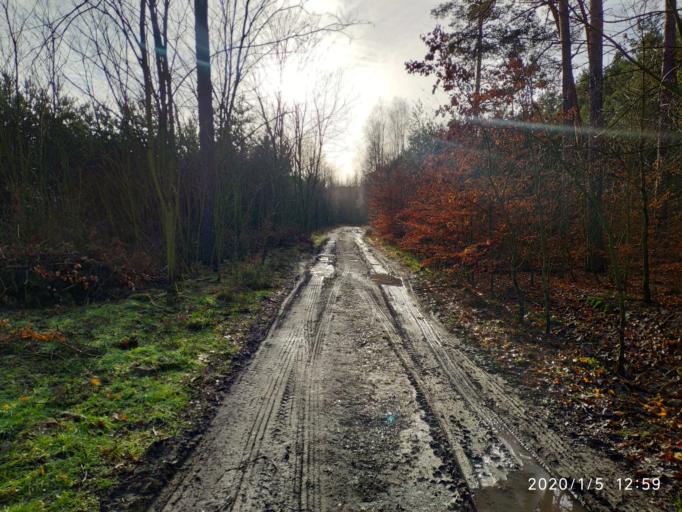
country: PL
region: Lubusz
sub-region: Powiat zielonogorski
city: Czerwiensk
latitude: 52.0175
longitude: 15.3780
